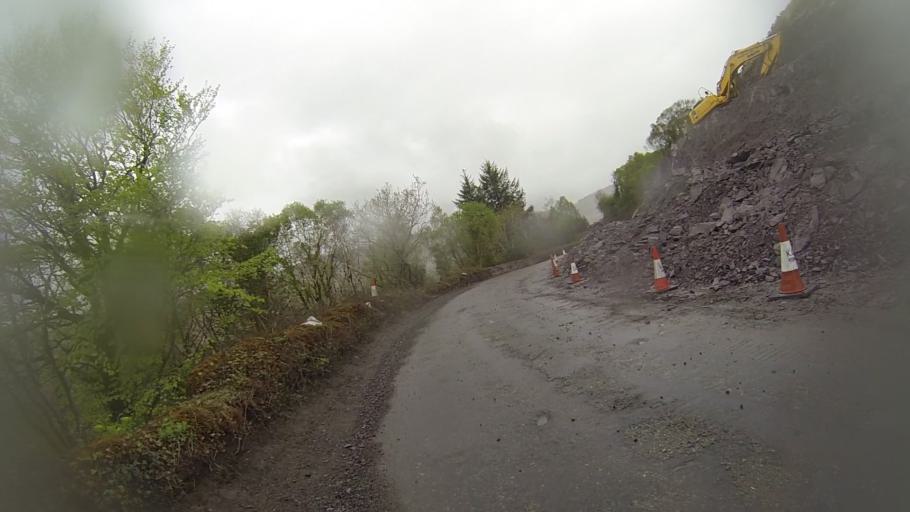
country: IE
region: Munster
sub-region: Ciarrai
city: Kenmare
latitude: 51.8060
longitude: -9.5570
